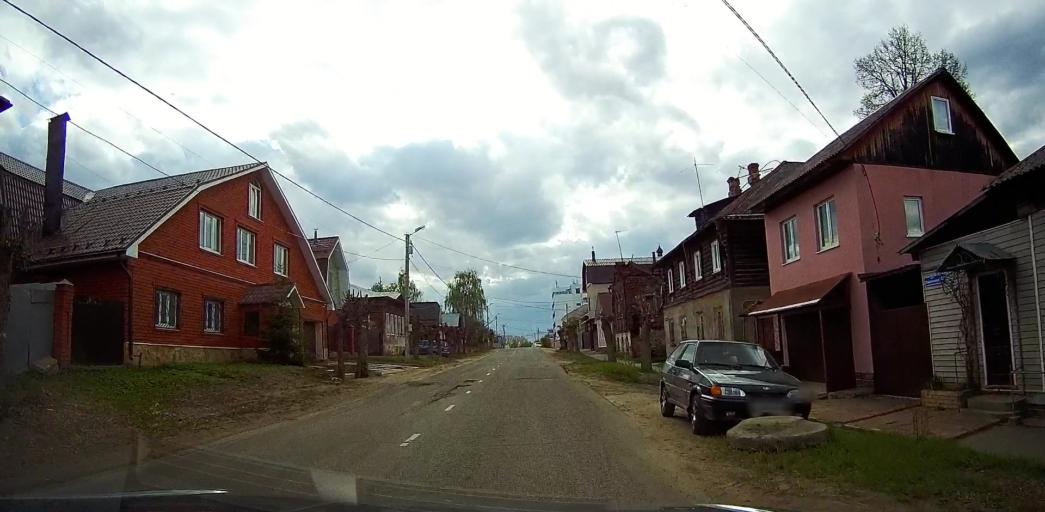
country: RU
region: Moskovskaya
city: Pavlovskiy Posad
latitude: 55.7816
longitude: 38.6555
